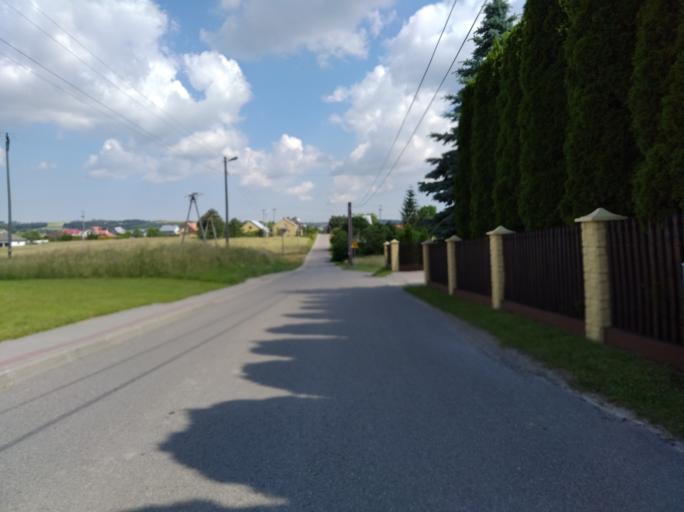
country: PL
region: Subcarpathian Voivodeship
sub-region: Powiat rzeszowski
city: Dynow
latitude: 49.8225
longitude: 22.2279
